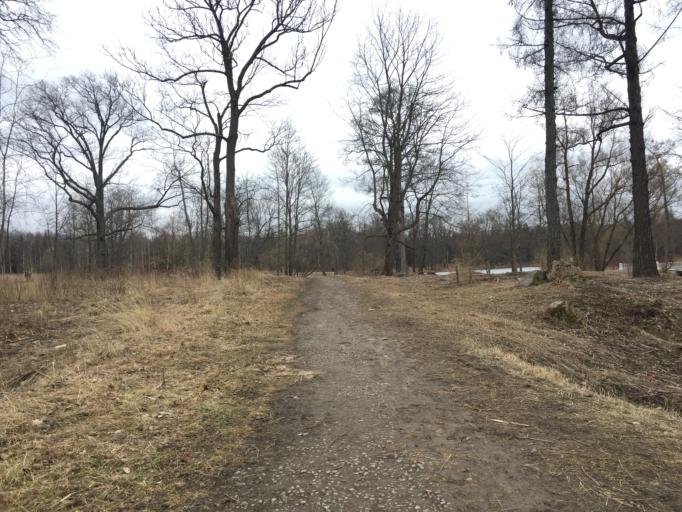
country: RU
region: St.-Petersburg
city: Pushkin
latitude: 59.7246
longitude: 30.3704
